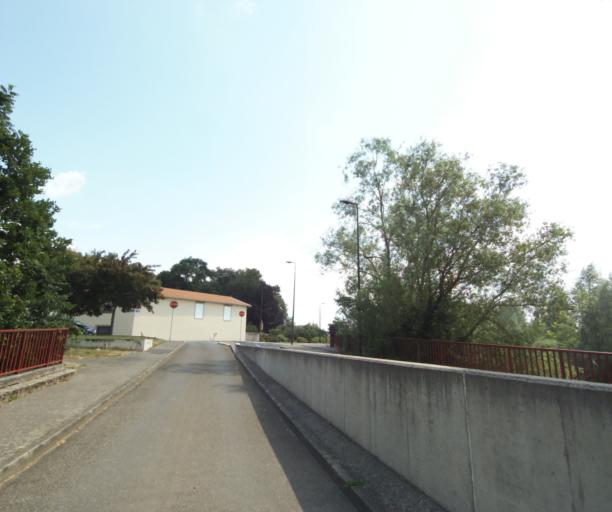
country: FR
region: Lorraine
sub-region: Departement de Meurthe-et-Moselle
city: Luneville
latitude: 48.5951
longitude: 6.4868
